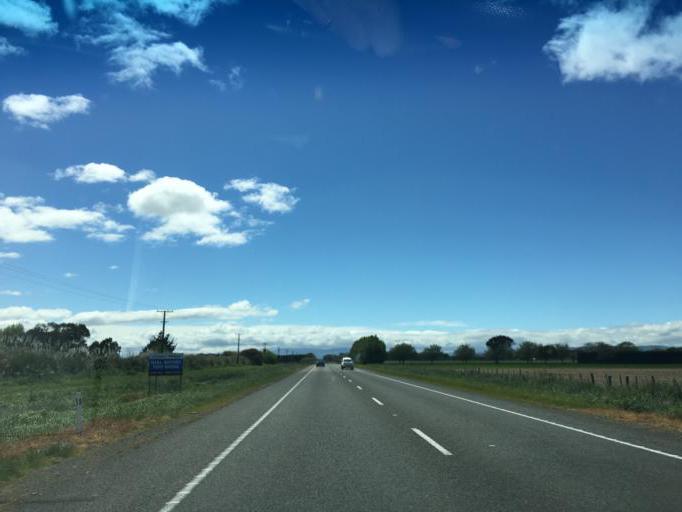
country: NZ
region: Manawatu-Wanganui
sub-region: Palmerston North City
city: Palmerston North
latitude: -40.4066
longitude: 175.4916
